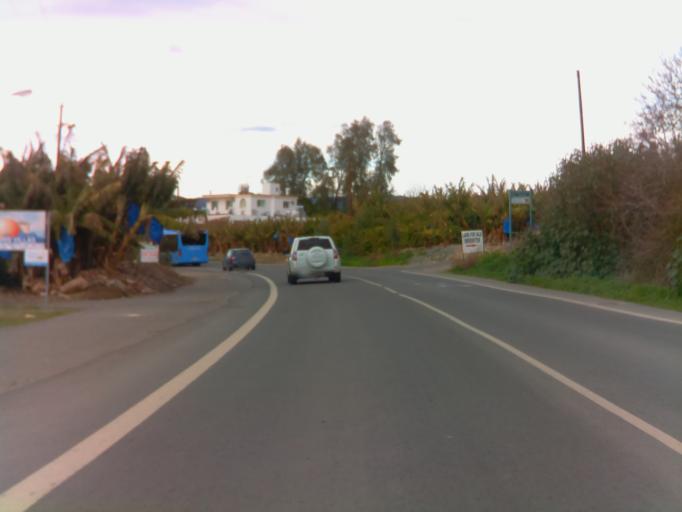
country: CY
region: Pafos
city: Kissonerga
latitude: 34.8188
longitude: 32.3951
